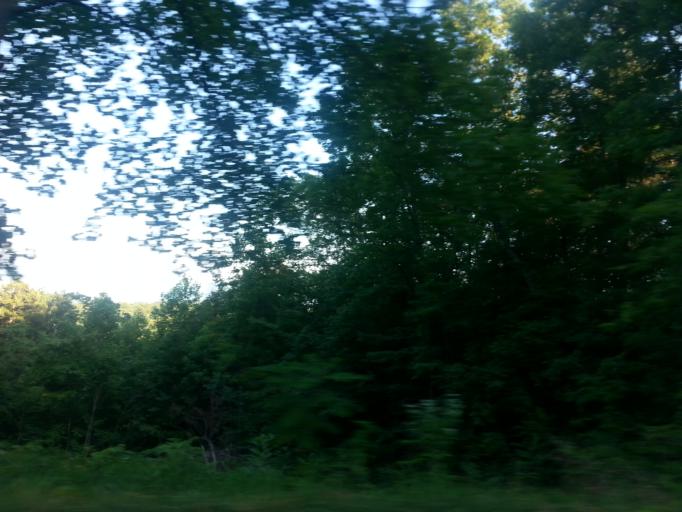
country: US
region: Tennessee
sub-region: Blount County
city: Maryville
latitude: 35.6384
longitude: -83.9307
